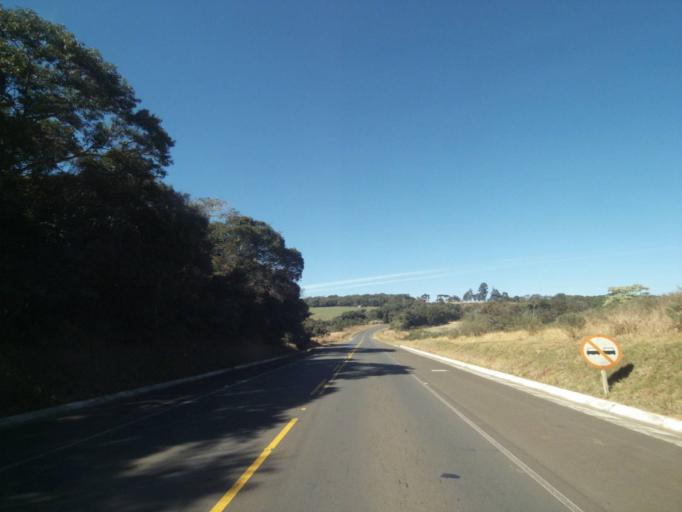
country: BR
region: Parana
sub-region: Tibagi
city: Tibagi
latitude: -24.7735
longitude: -50.4640
